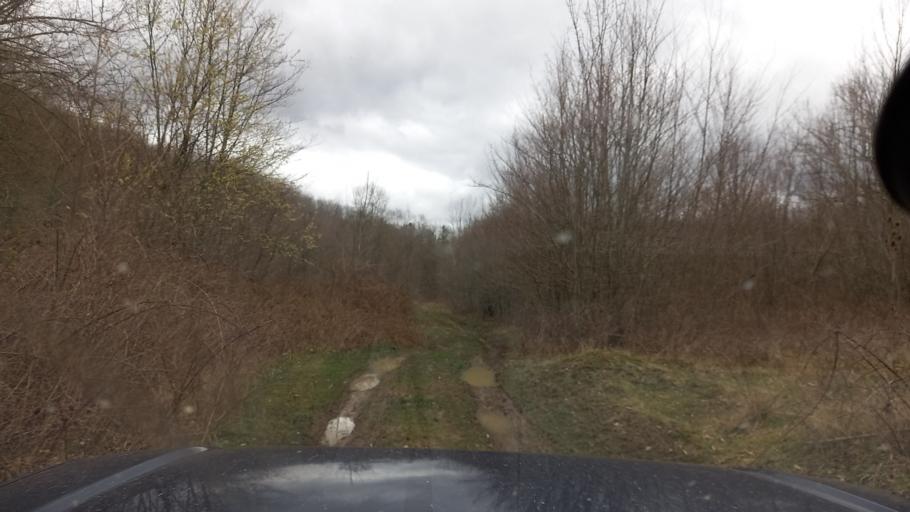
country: RU
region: Krasnodarskiy
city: Pshada
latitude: 44.4882
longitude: 38.3954
